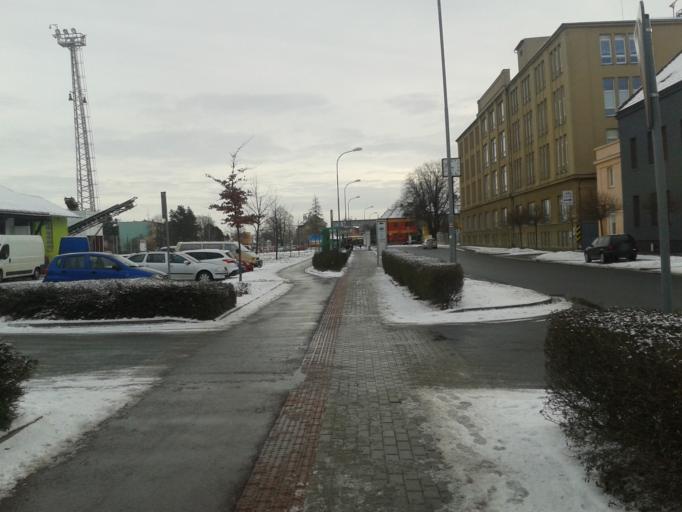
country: CZ
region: Olomoucky
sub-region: Okres Prostejov
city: Prostejov
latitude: 49.4782
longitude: 17.1119
